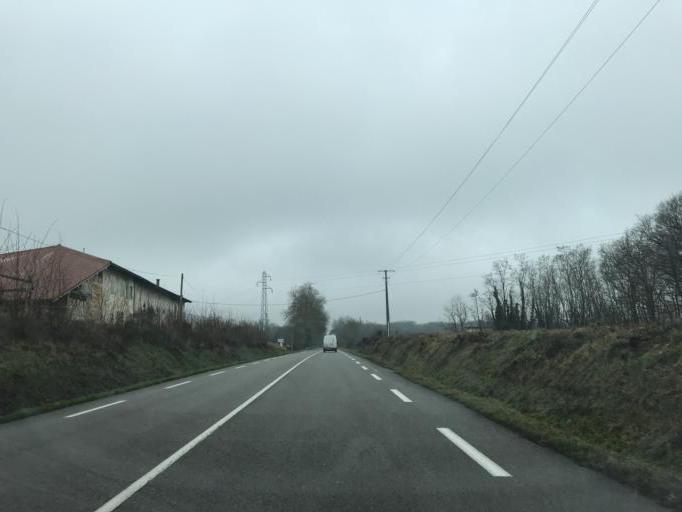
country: FR
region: Rhone-Alpes
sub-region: Departement de l'Ain
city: Servas
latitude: 46.1525
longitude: 5.1797
